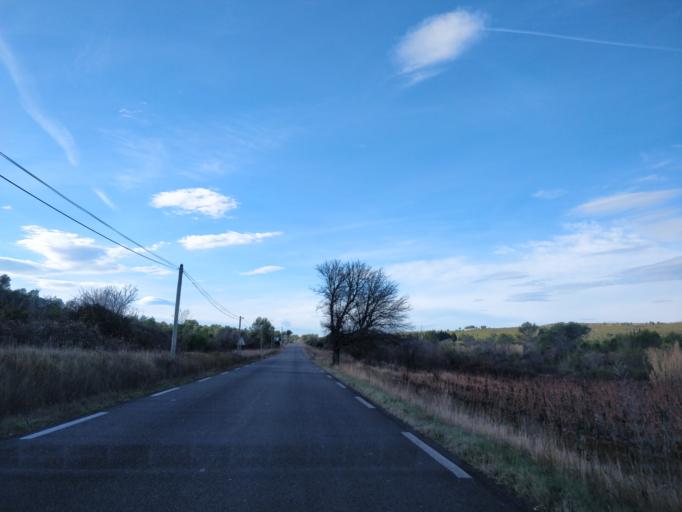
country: FR
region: Languedoc-Roussillon
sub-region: Departement de l'Herault
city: Saint-Drezery
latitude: 43.7264
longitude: 3.9589
